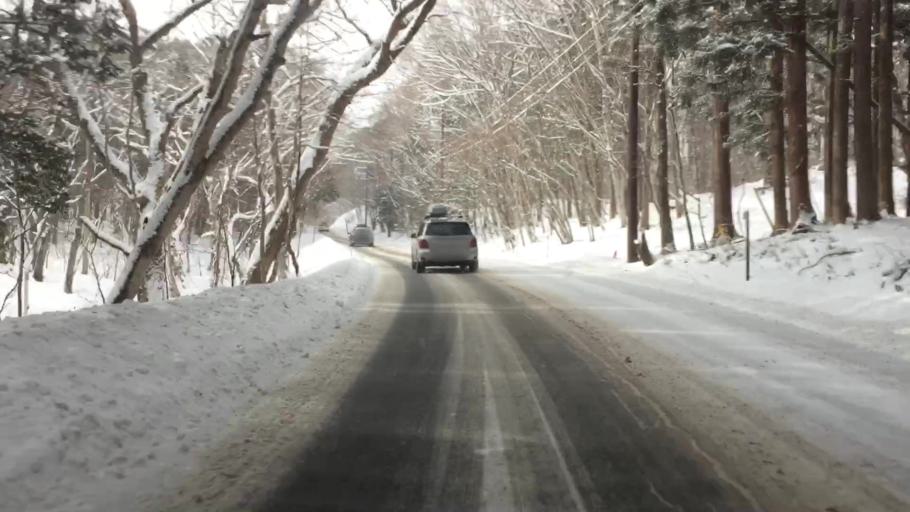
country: JP
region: Tochigi
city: Yaita
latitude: 36.9523
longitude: 139.7590
